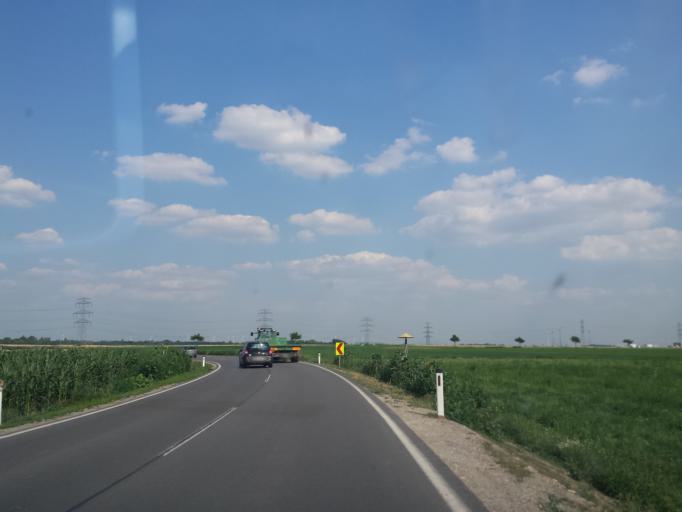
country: AT
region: Lower Austria
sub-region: Politischer Bezirk Ganserndorf
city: Aderklaa
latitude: 48.2820
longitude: 16.5506
